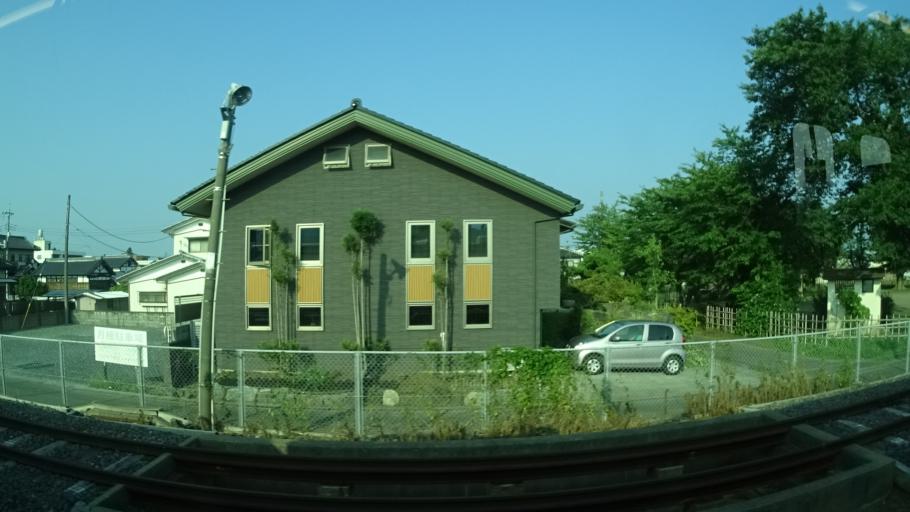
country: JP
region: Ibaraki
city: Hitachi
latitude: 36.6361
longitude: 140.6757
